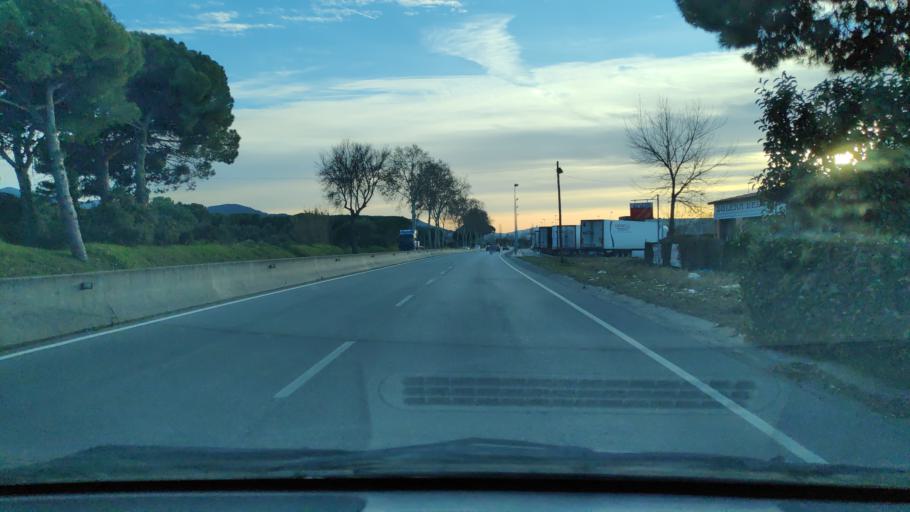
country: ES
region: Catalonia
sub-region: Provincia de Barcelona
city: Montmelo
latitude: 41.5693
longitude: 2.2683
